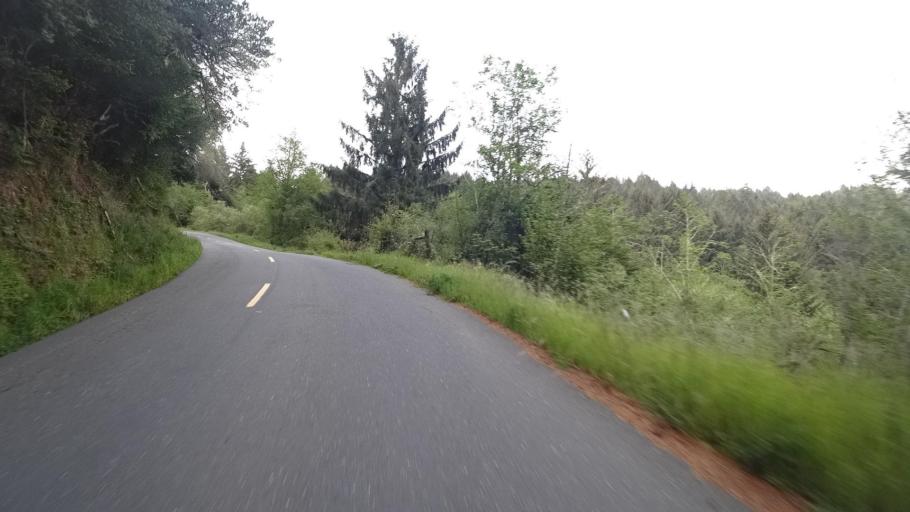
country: US
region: California
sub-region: Humboldt County
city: Ferndale
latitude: 40.5468
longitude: -124.2762
